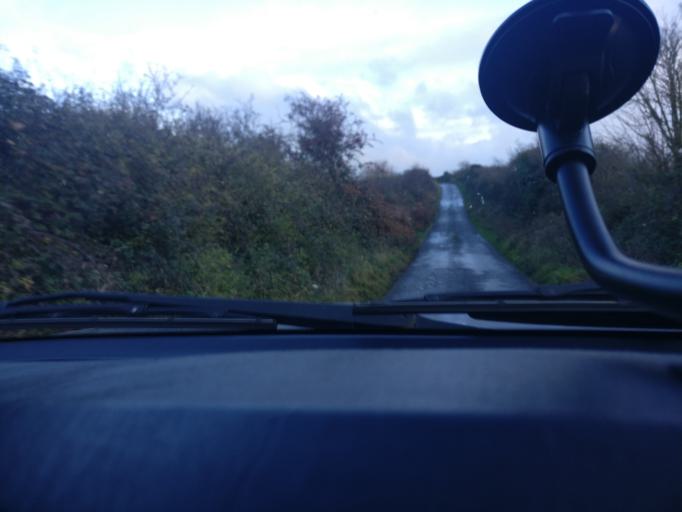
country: IE
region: Connaught
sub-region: County Galway
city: Athenry
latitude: 53.1976
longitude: -8.6914
